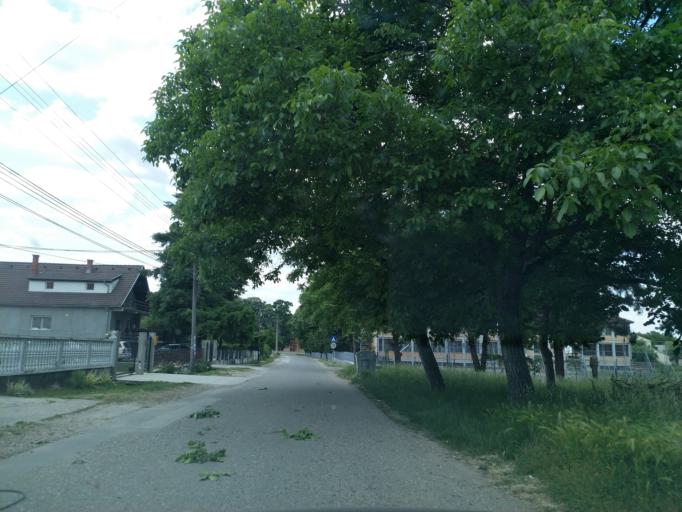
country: RS
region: Central Serbia
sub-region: Pomoravski Okrug
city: Jagodina
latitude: 43.9439
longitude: 21.2974
